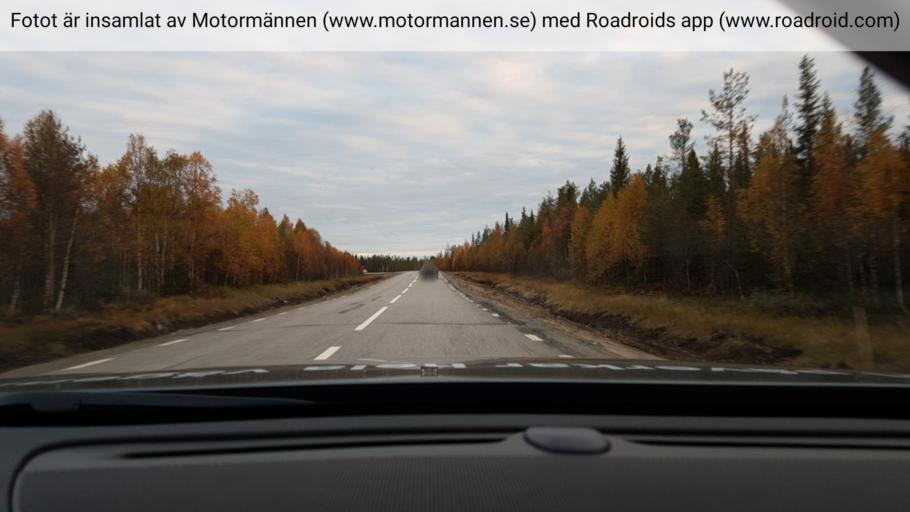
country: SE
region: Norrbotten
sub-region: Jokkmokks Kommun
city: Jokkmokk
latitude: 66.1063
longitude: 20.0558
